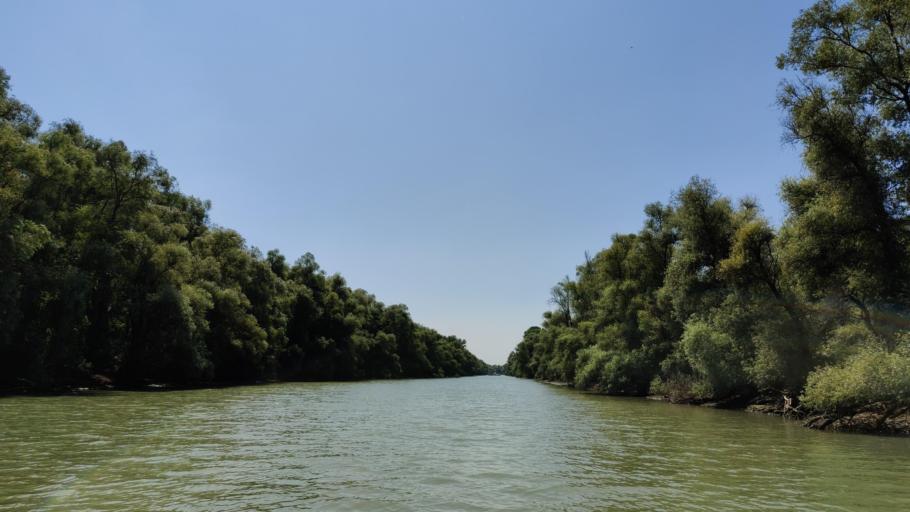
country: RO
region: Tulcea
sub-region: Comuna Pardina
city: Pardina
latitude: 45.2505
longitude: 28.9250
